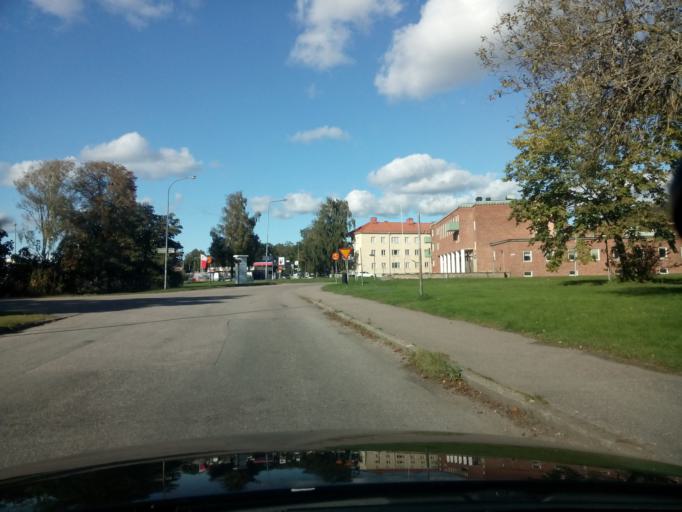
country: SE
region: Soedermanland
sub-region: Nykopings Kommun
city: Nykoping
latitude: 58.7466
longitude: 17.0022
